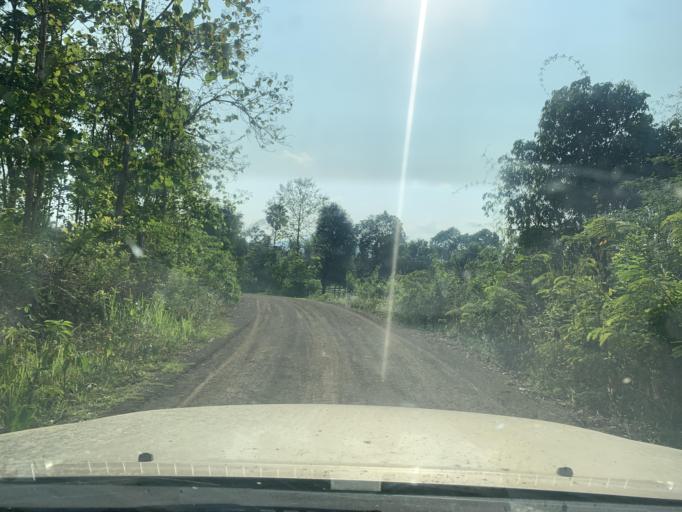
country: TH
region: Uttaradit
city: Ban Khok
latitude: 18.2877
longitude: 101.3215
